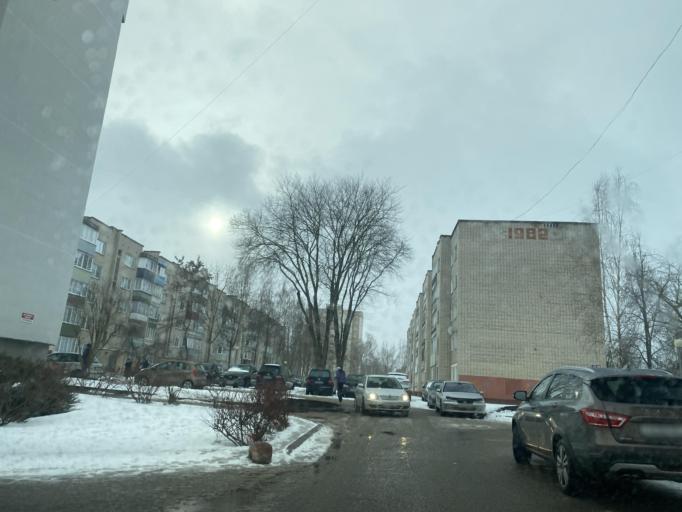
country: BY
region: Minsk
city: Horad Zhodzina
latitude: 54.0937
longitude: 28.3065
